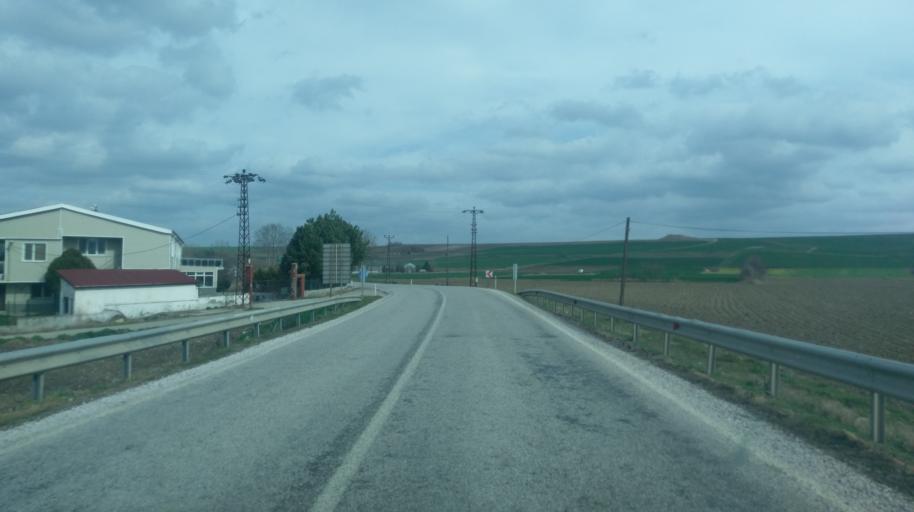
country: TR
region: Edirne
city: Haskoy
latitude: 41.6425
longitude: 26.8644
